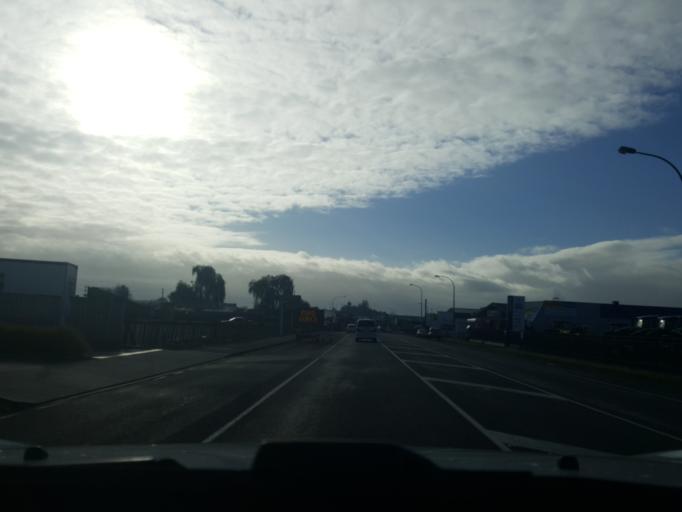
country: NZ
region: Waikato
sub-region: Waipa District
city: Cambridge
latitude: -37.6600
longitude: 175.5224
